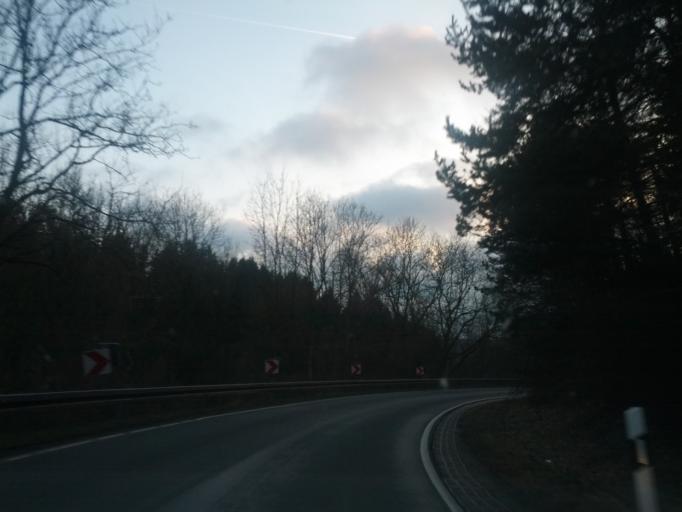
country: DE
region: Thuringia
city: Katharinenberg
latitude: 51.1734
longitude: 10.2705
